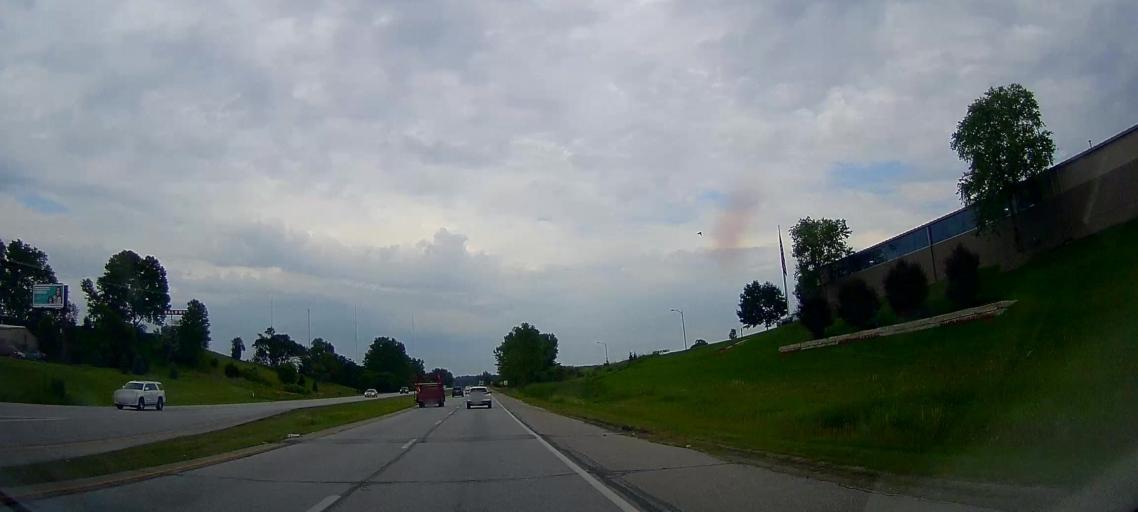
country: US
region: Nebraska
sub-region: Douglas County
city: Bennington
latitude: 41.3184
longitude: -96.0638
